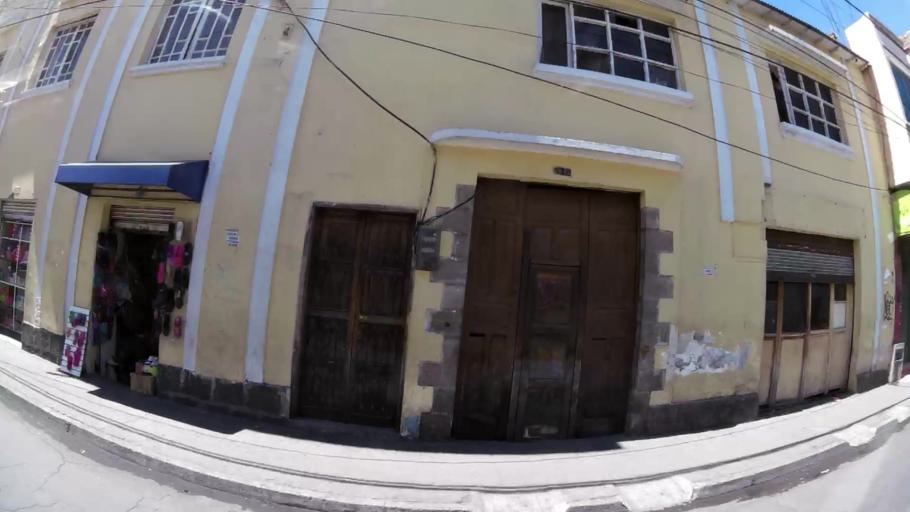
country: EC
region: Chimborazo
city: Riobamba
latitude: -1.6715
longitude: -78.6549
